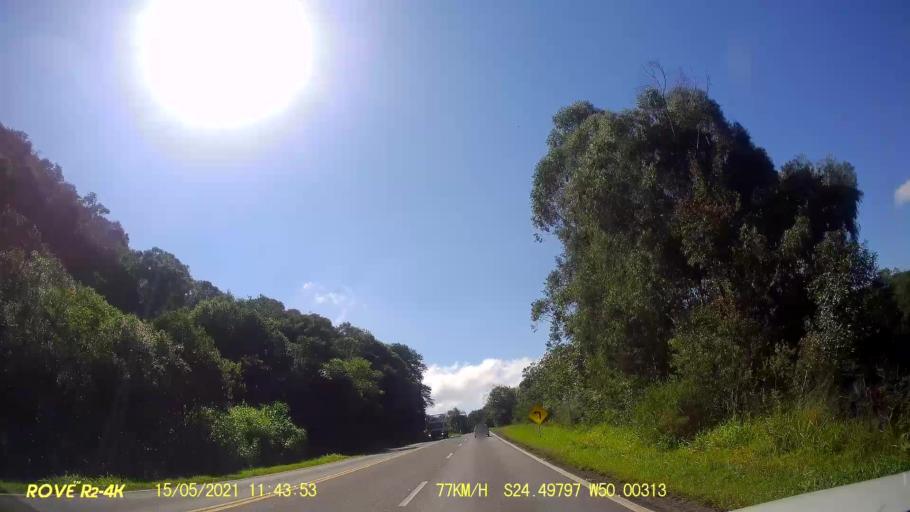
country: BR
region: Parana
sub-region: Pirai Do Sul
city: Pirai do Sul
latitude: -24.4980
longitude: -50.0031
